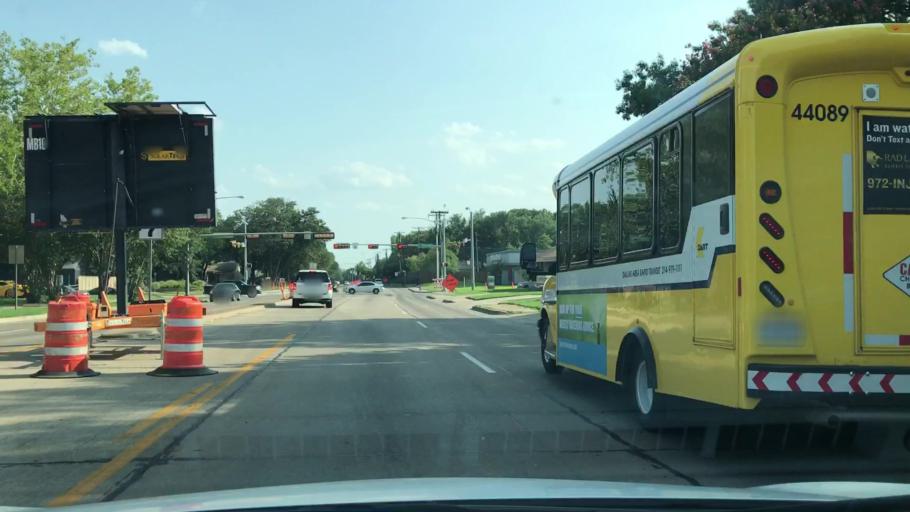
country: US
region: Texas
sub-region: Dallas County
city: Irving
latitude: 32.8303
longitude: -96.9512
